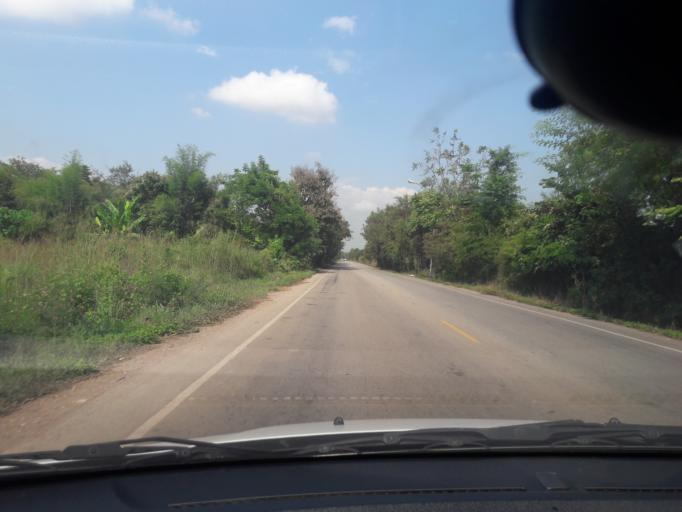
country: TH
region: Lampang
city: Mae Tha
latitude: 18.2004
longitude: 99.5064
